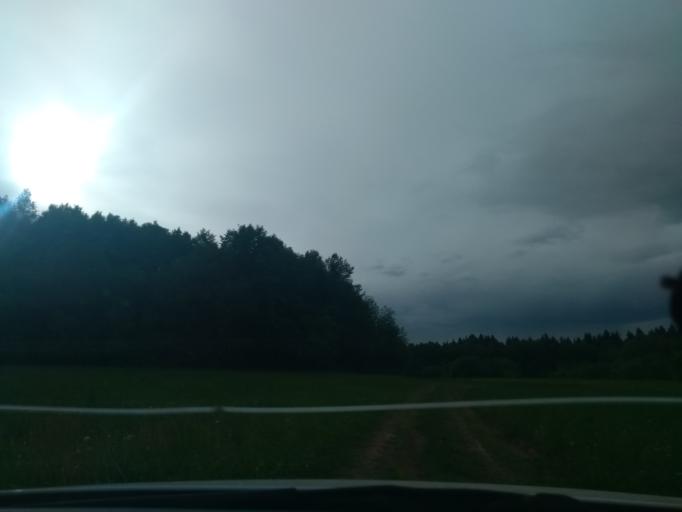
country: RU
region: Perm
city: Ferma
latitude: 57.9809
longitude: 56.3366
